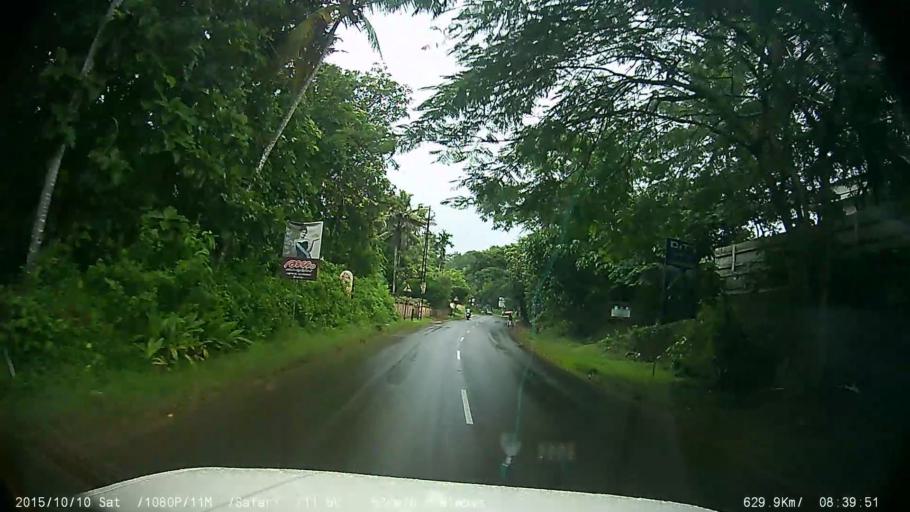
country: IN
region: Kerala
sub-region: Kottayam
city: Palackattumala
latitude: 9.7567
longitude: 76.5548
